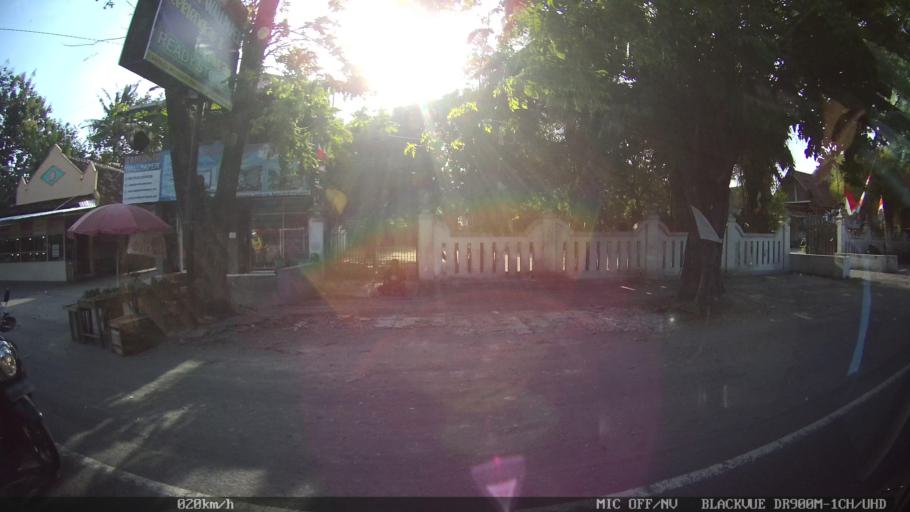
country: ID
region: Daerah Istimewa Yogyakarta
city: Bantul
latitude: -7.8703
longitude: 110.3370
